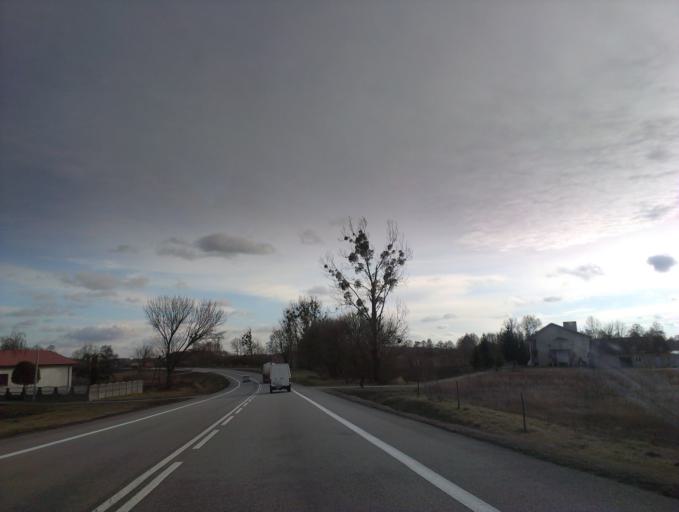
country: PL
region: Kujawsko-Pomorskie
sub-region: Powiat lipnowski
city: Kikol
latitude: 52.9209
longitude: 19.0961
